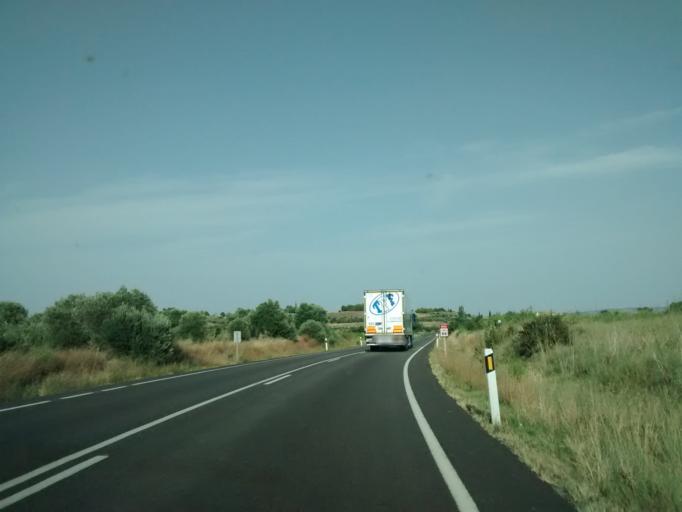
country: ES
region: Aragon
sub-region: Provincia de Zaragoza
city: Malejan
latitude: 41.8302
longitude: -1.5633
